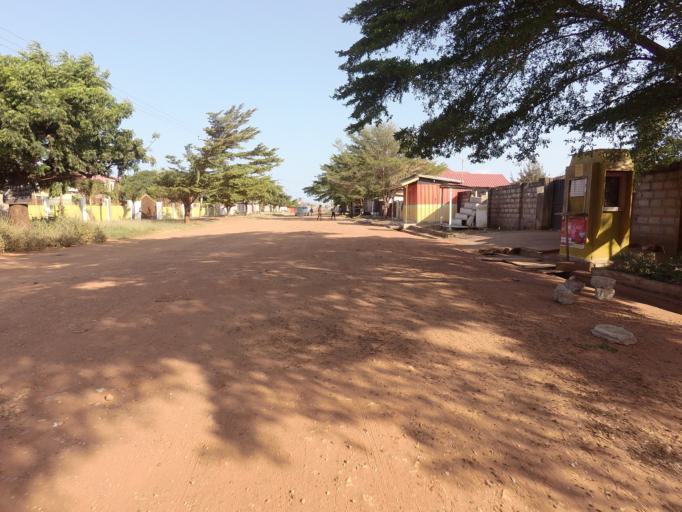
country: GH
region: Greater Accra
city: Nungua
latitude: 5.6374
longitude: -0.0854
